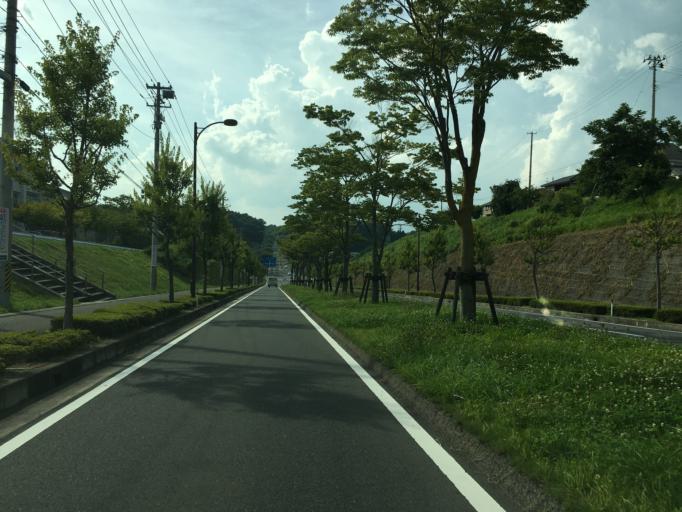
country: JP
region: Fukushima
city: Koriyama
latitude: 37.3898
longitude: 140.4318
